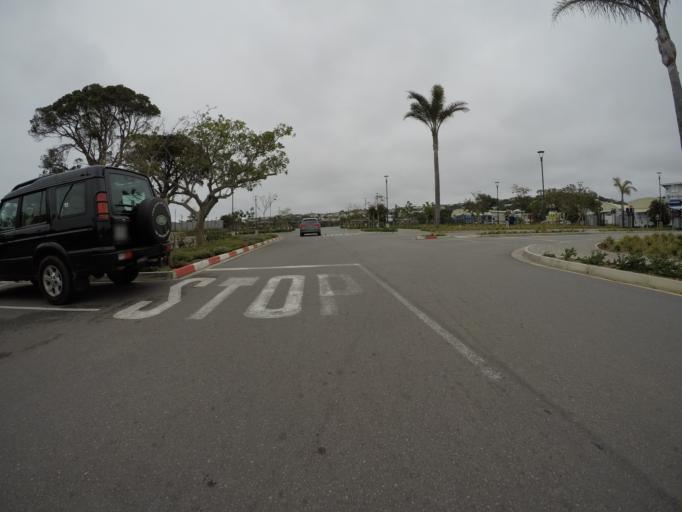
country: ZA
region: Western Cape
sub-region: Eden District Municipality
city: Plettenberg Bay
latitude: -34.0426
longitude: 23.3713
